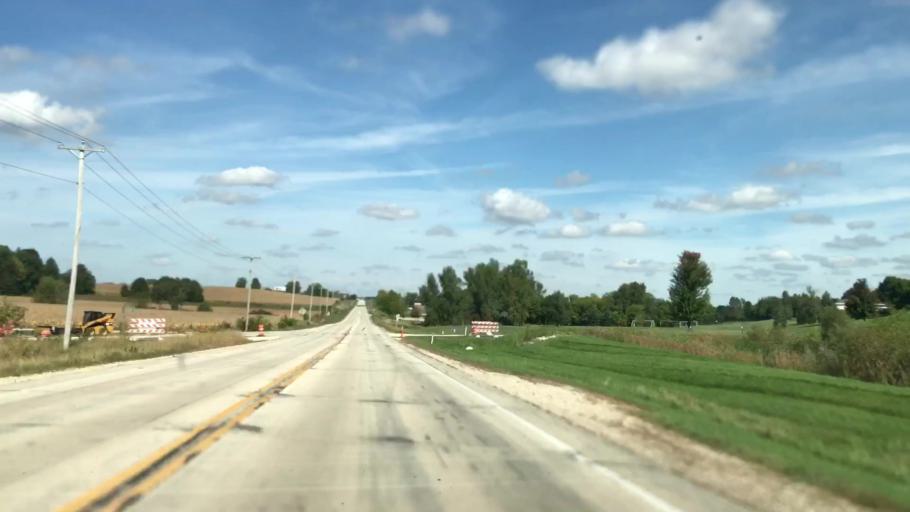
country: US
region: Wisconsin
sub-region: Dodge County
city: Mayville
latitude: 43.4935
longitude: -88.5710
